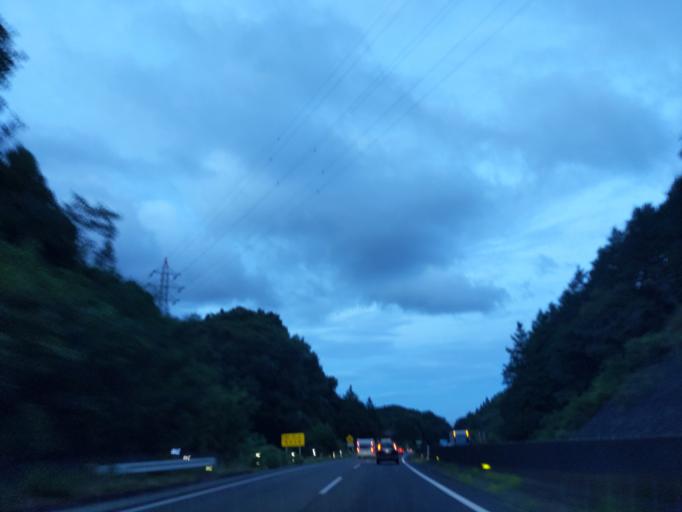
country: JP
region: Fukushima
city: Sukagawa
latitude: 37.1482
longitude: 140.2057
